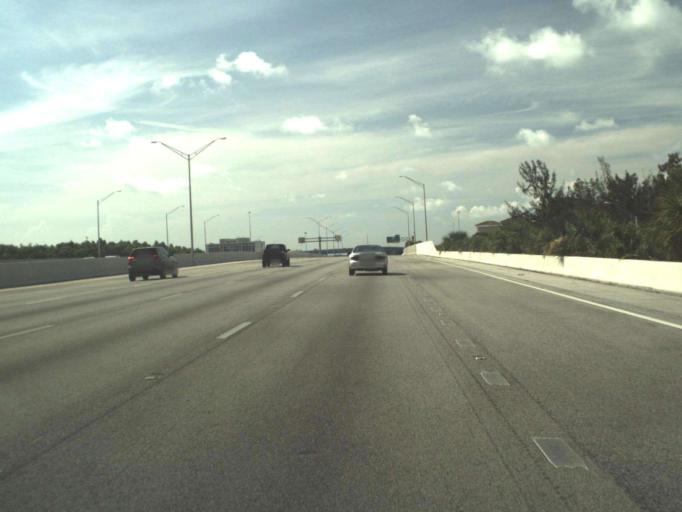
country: US
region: Florida
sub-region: Palm Beach County
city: North Palm Beach
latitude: 26.8464
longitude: -80.1065
